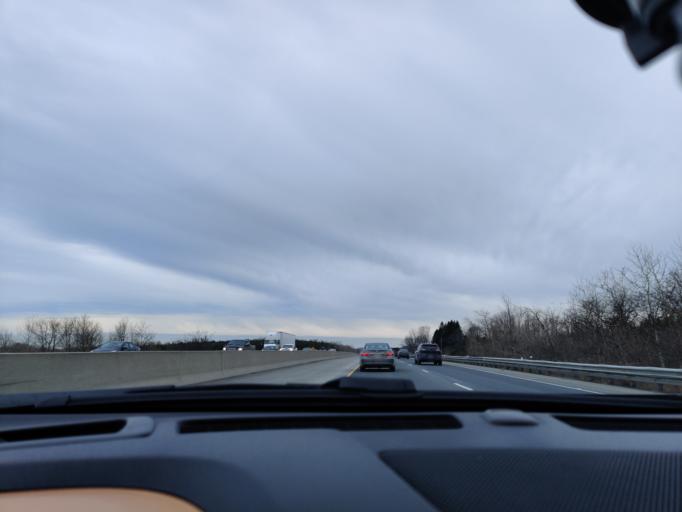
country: CA
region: Ontario
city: Cobourg
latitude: 44.0146
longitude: -77.9652
